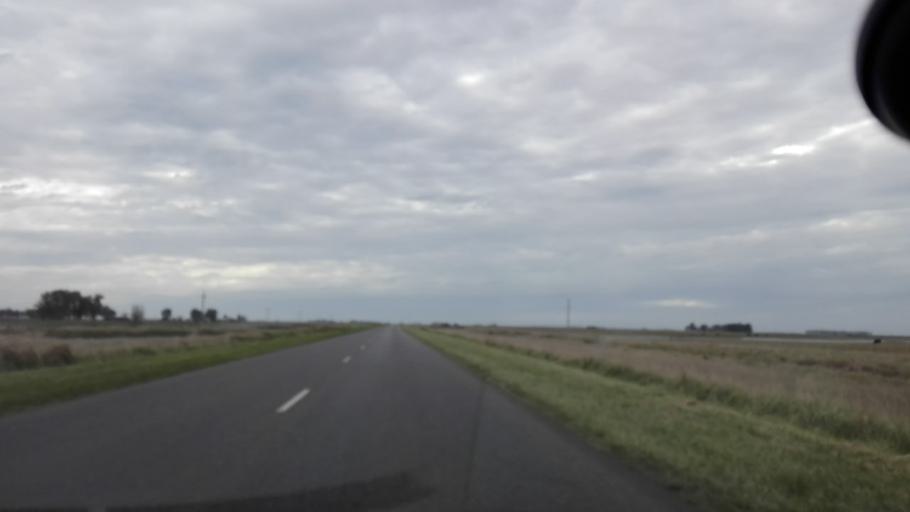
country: AR
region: Buenos Aires
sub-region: Partido de Las Flores
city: Las Flores
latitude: -36.3908
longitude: -59.0012
